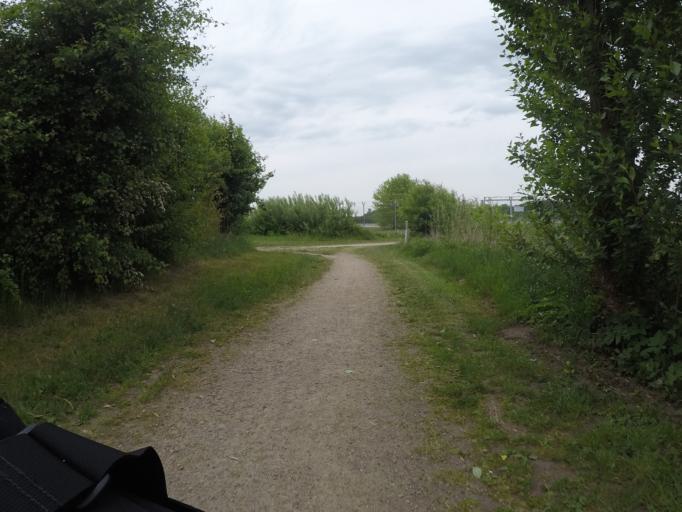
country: DE
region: Hamburg
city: Langenhorn
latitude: 53.6436
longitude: 9.9810
